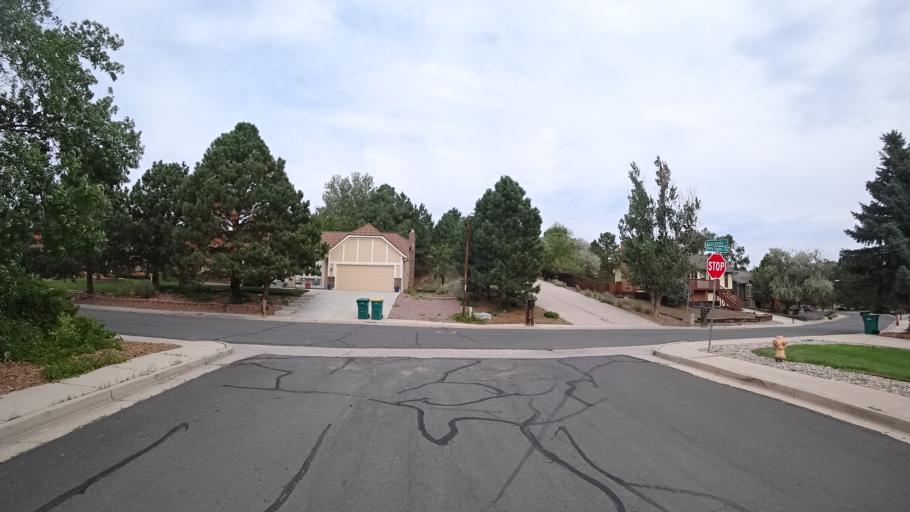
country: US
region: Colorado
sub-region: El Paso County
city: Air Force Academy
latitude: 38.9277
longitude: -104.8386
